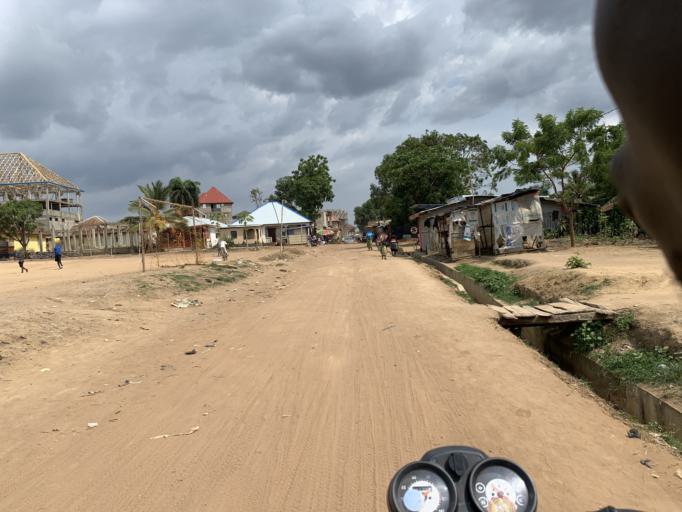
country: SL
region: Western Area
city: Waterloo
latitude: 8.3315
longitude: -13.0528
